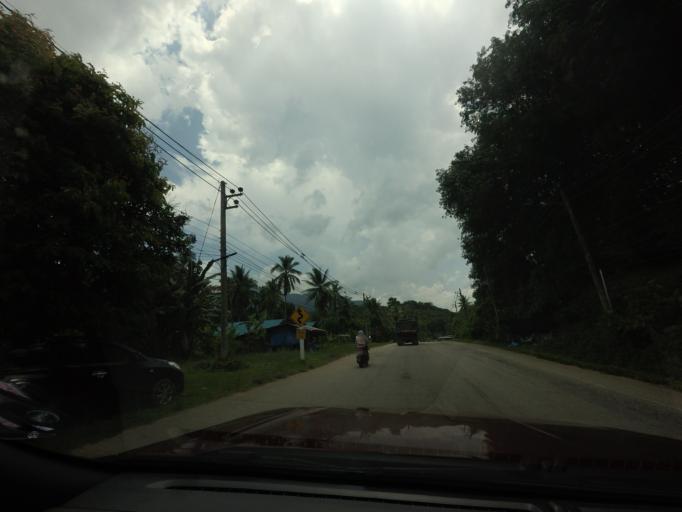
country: TH
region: Yala
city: Than To
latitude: 6.0720
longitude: 101.1936
